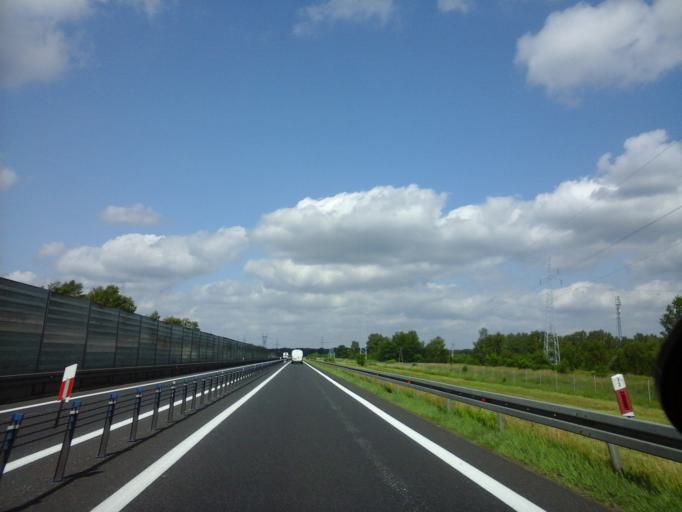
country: PL
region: West Pomeranian Voivodeship
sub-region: Powiat stargardzki
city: Kobylanka
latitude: 53.3584
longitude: 14.9217
